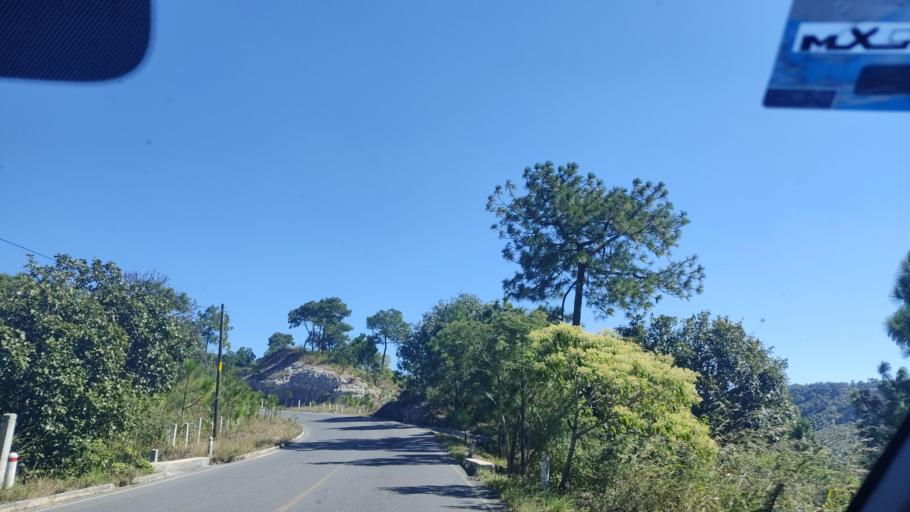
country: MX
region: Nayarit
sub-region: Jala
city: Rosa Blanca
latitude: 21.1014
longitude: -104.3719
